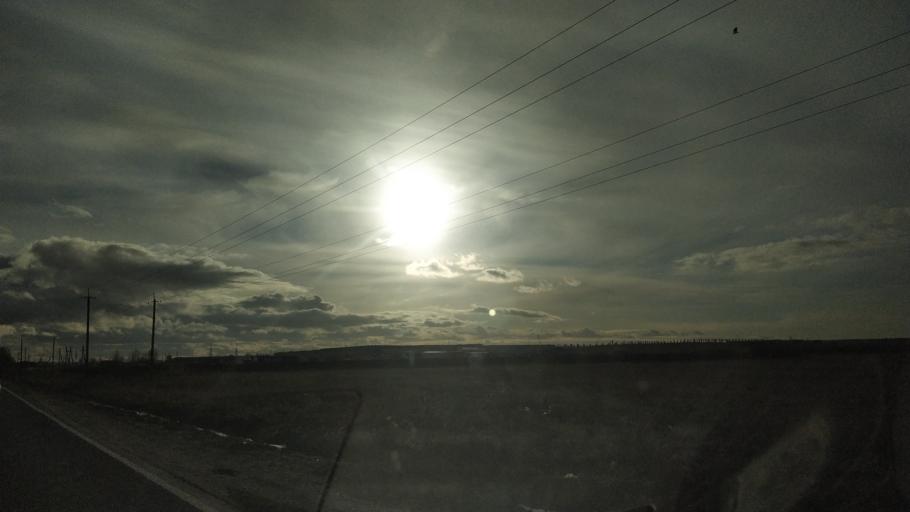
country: RU
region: St.-Petersburg
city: Petro-Slavyanka
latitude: 59.7762
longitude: 30.4776
